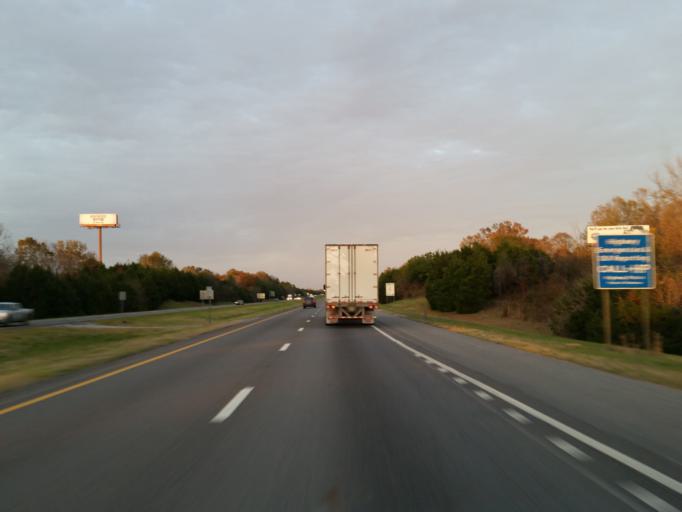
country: US
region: Alabama
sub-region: Sumter County
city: Livingston
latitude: 32.6314
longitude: -88.2049
